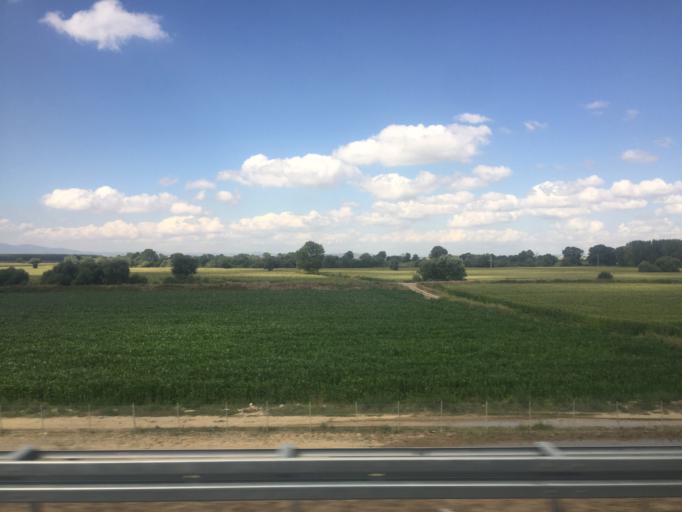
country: TR
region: Bursa
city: Tatkavakli
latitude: 40.1084
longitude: 28.2772
